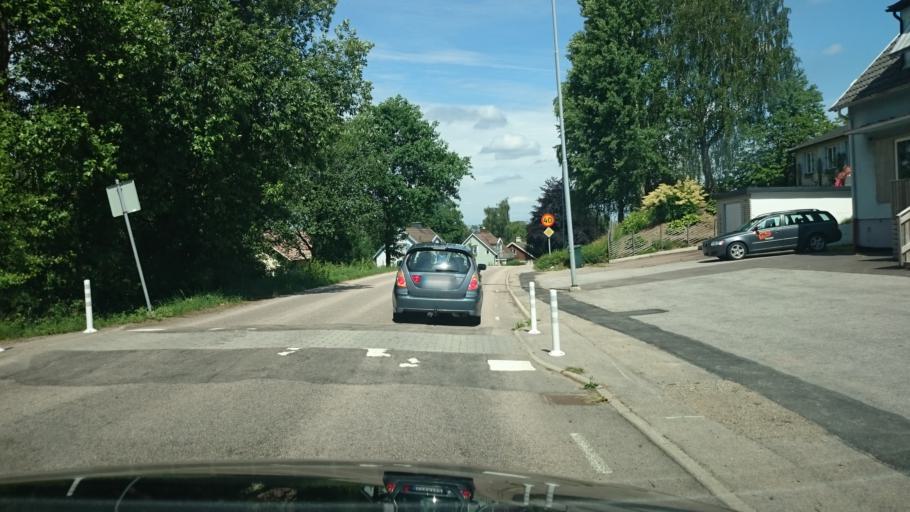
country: SE
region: Halland
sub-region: Hylte Kommun
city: Hyltebruk
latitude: 56.9914
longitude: 13.2359
